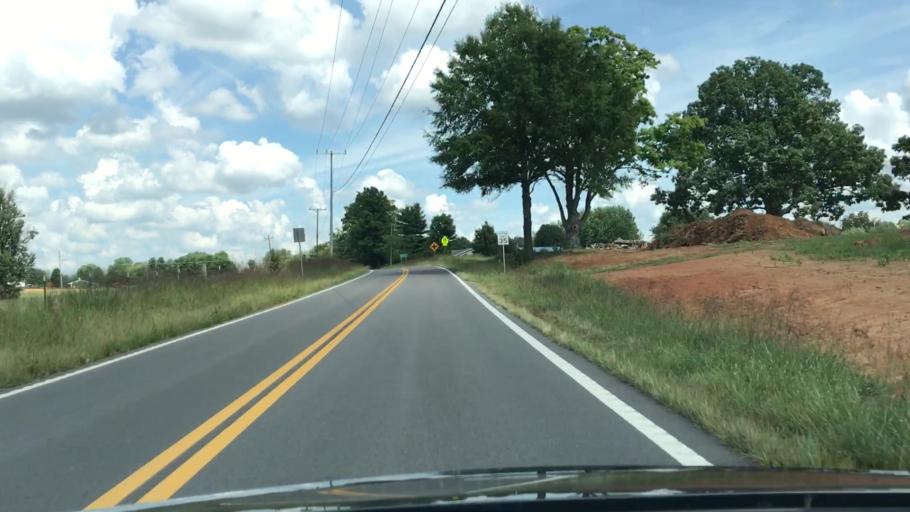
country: US
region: Tennessee
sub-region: Sumner County
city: White House
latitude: 36.5054
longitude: -86.5773
